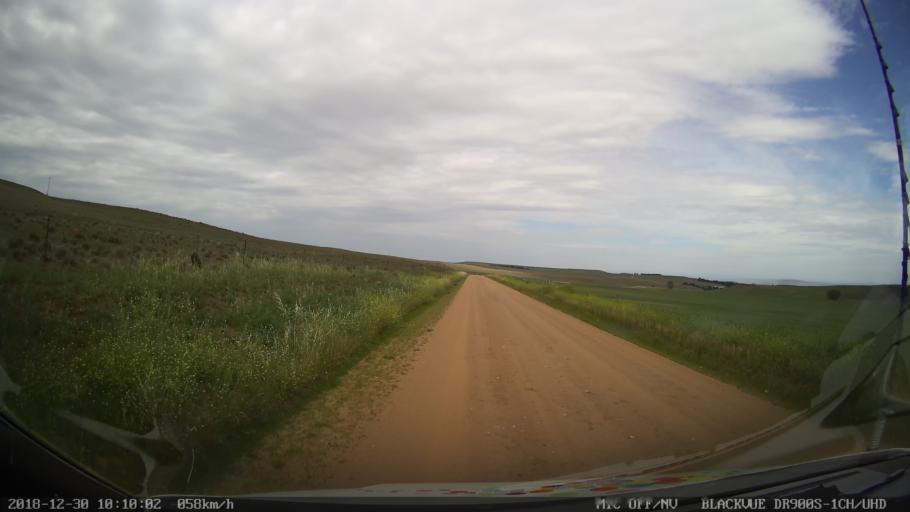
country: AU
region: New South Wales
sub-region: Cooma-Monaro
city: Cooma
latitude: -36.5501
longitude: 149.0991
